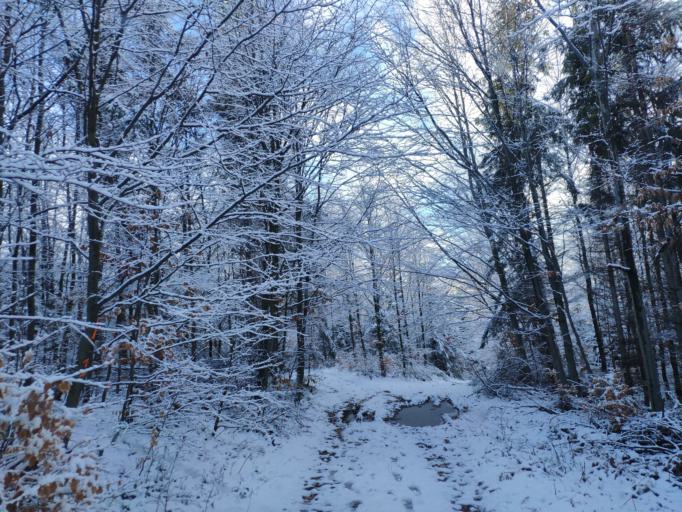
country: SK
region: Kosicky
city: Moldava nad Bodvou
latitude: 48.7428
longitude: 21.0929
